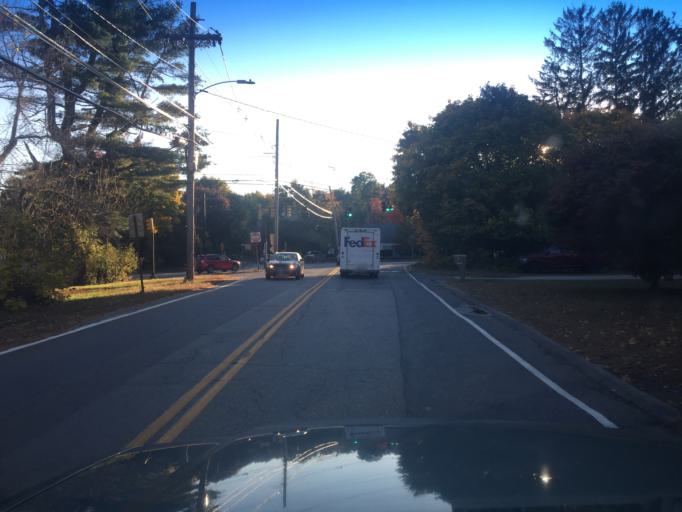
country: US
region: Massachusetts
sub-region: Middlesex County
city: Hudson
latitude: 42.3943
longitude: -71.5386
